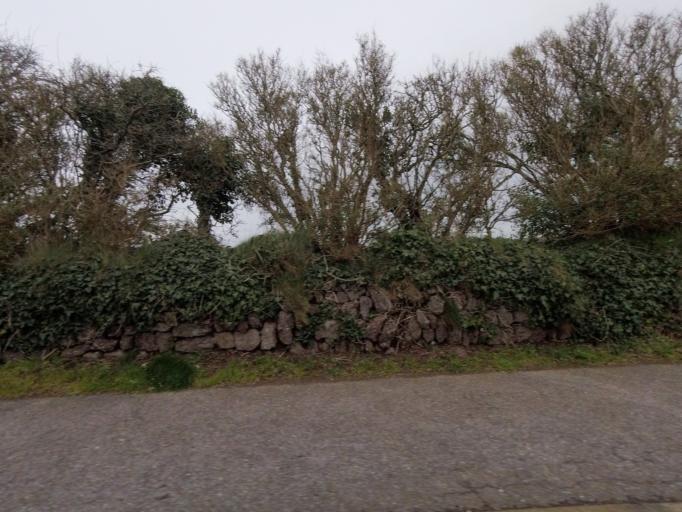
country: IE
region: Munster
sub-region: Waterford
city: Dunmore East
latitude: 52.1453
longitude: -6.9970
